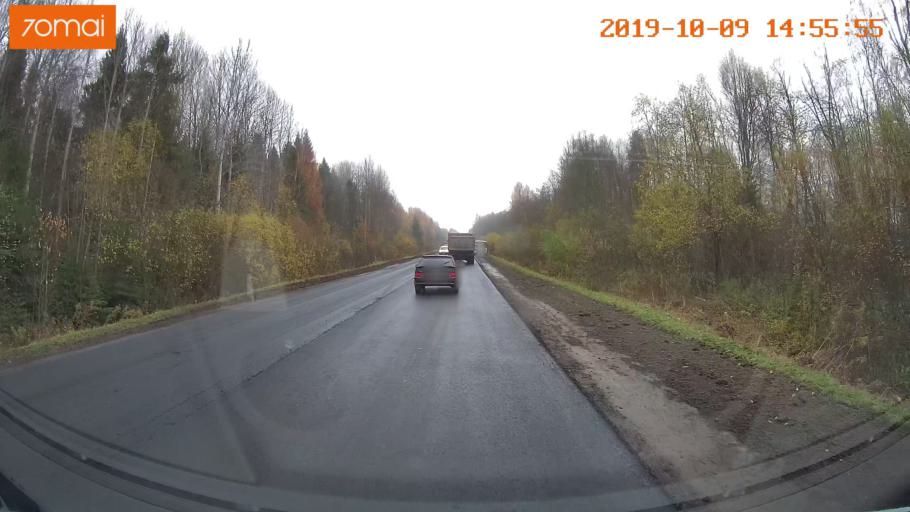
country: RU
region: Kostroma
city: Chistyye Bory
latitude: 58.3485
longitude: 41.6462
